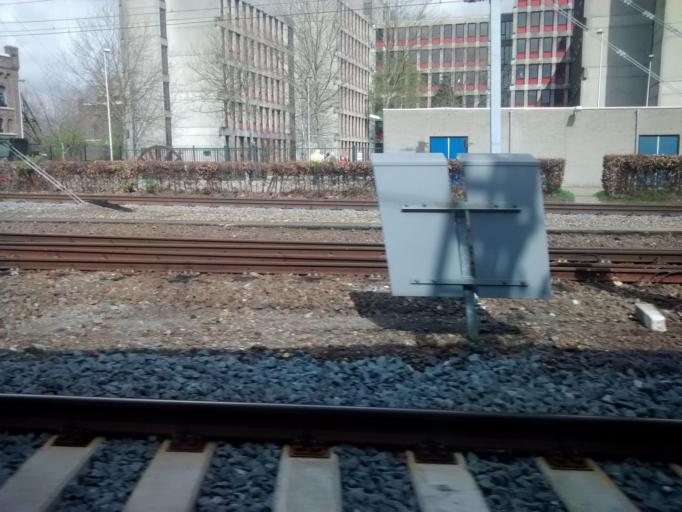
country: NL
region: Limburg
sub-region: Gemeente Heerlen
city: Heerlen
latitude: 50.8917
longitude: 5.9707
